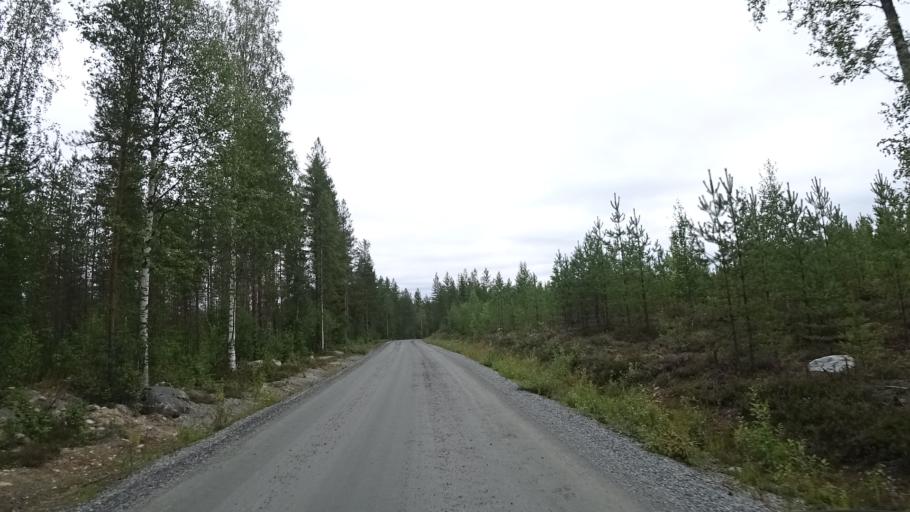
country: FI
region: North Karelia
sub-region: Pielisen Karjala
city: Lieksa
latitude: 63.3666
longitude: 30.3877
